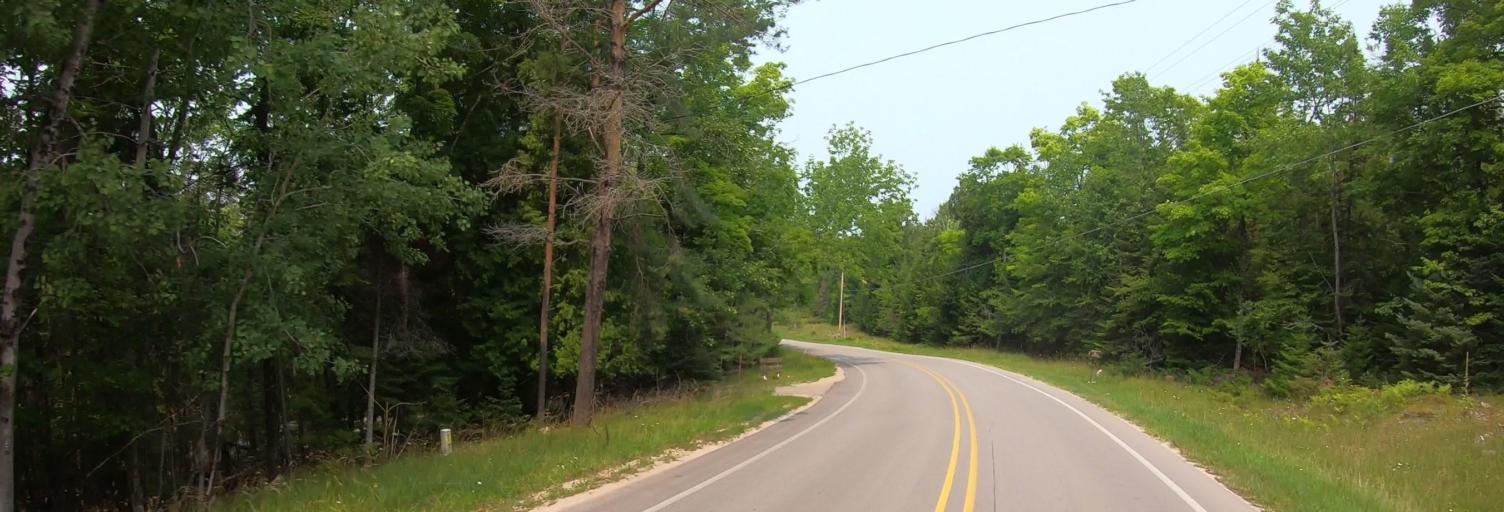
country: CA
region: Ontario
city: Thessalon
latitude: 46.0297
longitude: -83.7291
